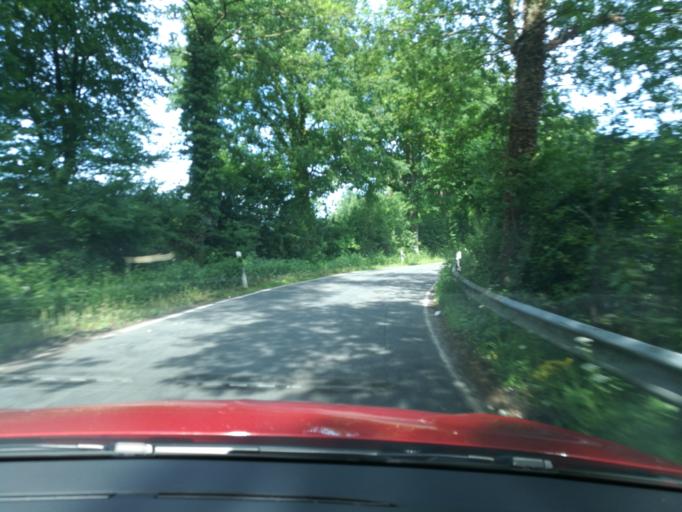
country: DE
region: Schleswig-Holstein
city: Tremsbuttel
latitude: 53.7445
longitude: 10.3374
